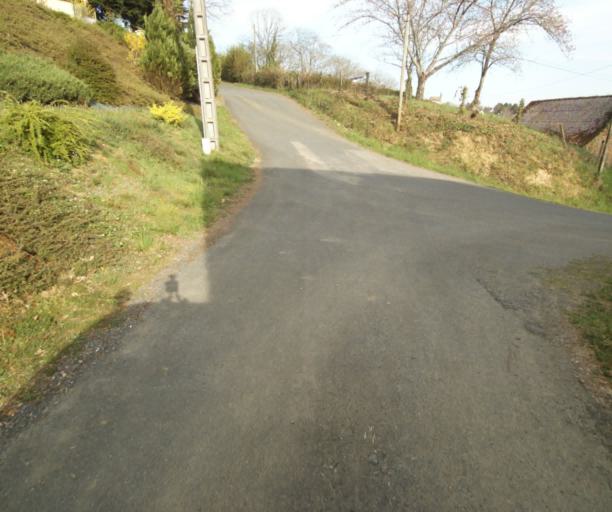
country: FR
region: Limousin
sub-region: Departement de la Correze
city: Naves
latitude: 45.3218
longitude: 1.7536
